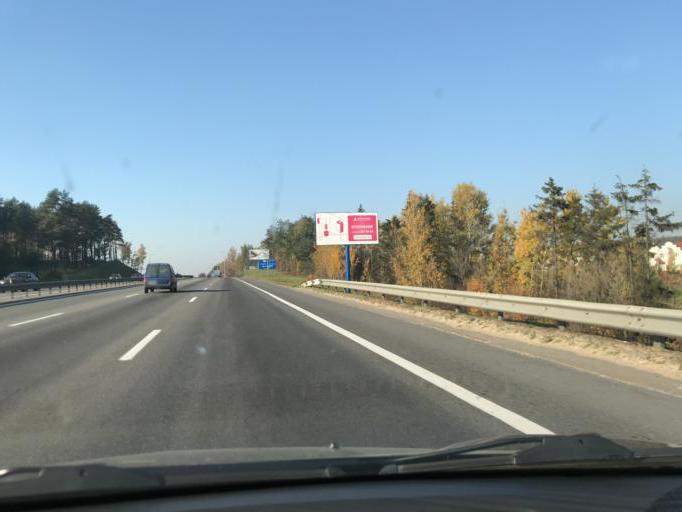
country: BY
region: Minsk
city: Pryvol'ny
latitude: 53.8168
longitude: 27.7699
